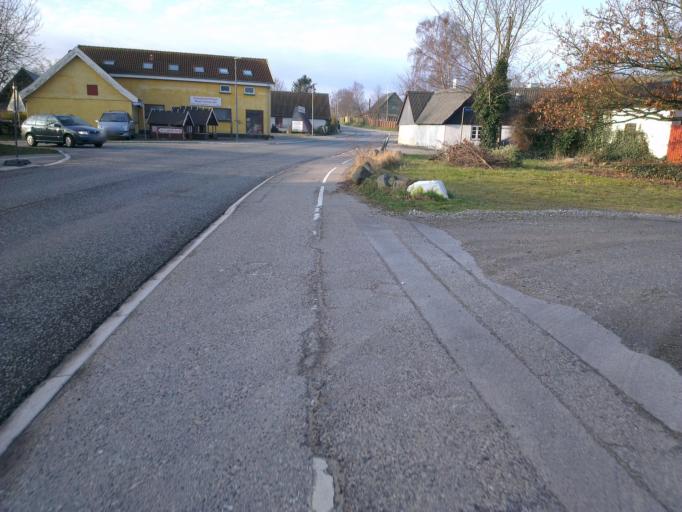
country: DK
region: Capital Region
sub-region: Frederikssund Kommune
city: Jaegerspris
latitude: 55.8250
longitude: 11.9886
